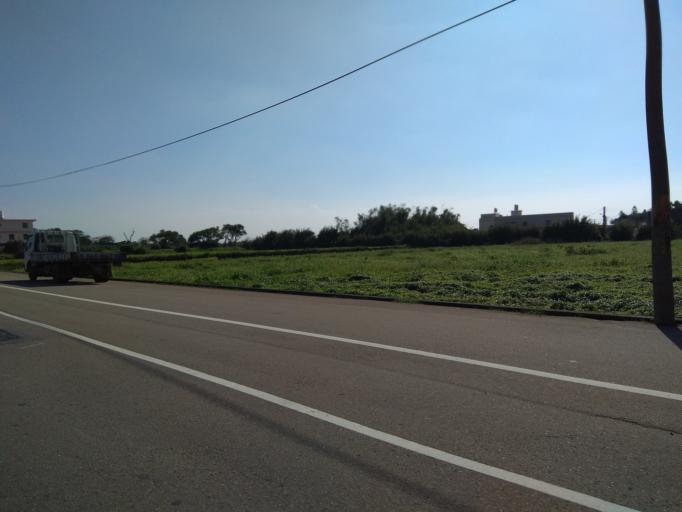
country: TW
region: Taiwan
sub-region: Hsinchu
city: Zhubei
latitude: 25.0302
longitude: 121.0765
